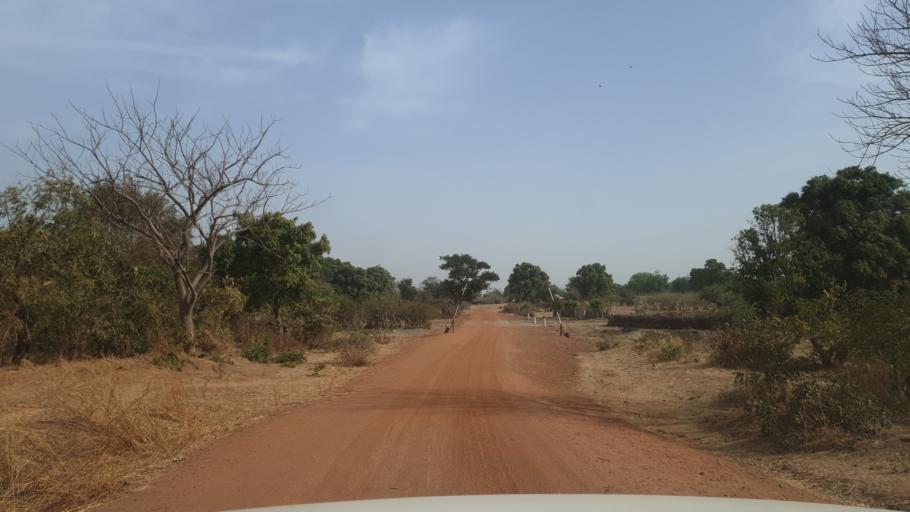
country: ML
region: Koulikoro
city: Kolokani
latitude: 13.3166
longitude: -8.2776
